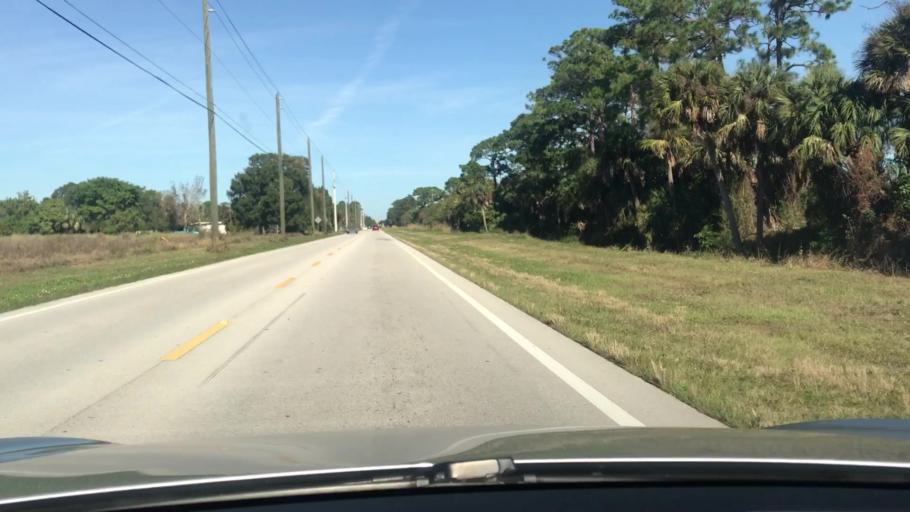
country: US
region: Florida
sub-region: Indian River County
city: Winter Beach
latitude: 27.7214
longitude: -80.4625
